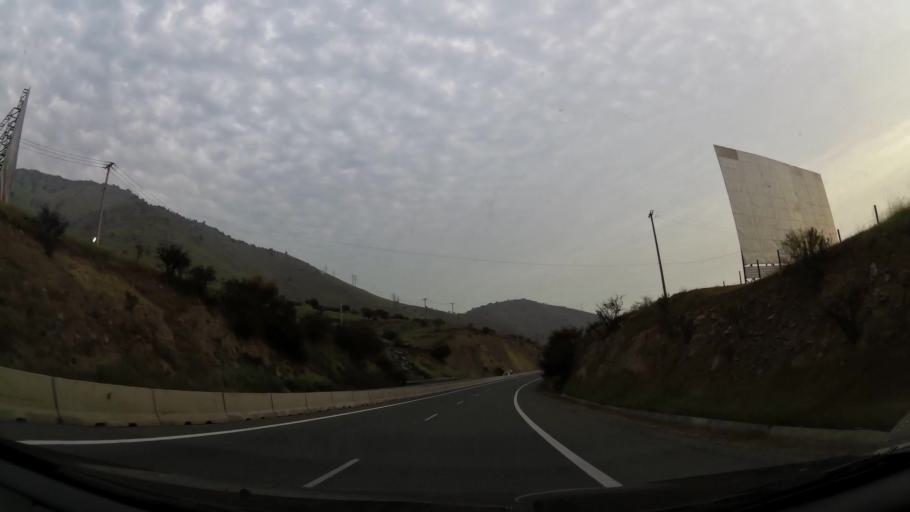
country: CL
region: Santiago Metropolitan
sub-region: Provincia de Chacabuco
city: Chicureo Abajo
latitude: -33.3557
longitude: -70.6143
